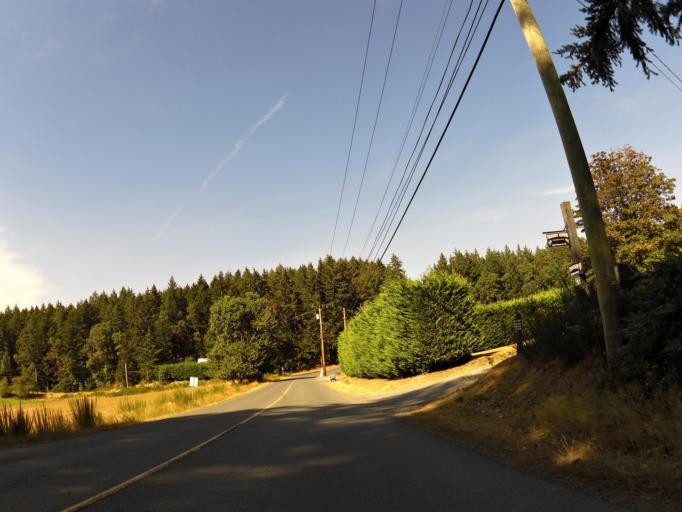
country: CA
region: British Columbia
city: North Saanich
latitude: 48.6703
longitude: -123.5535
